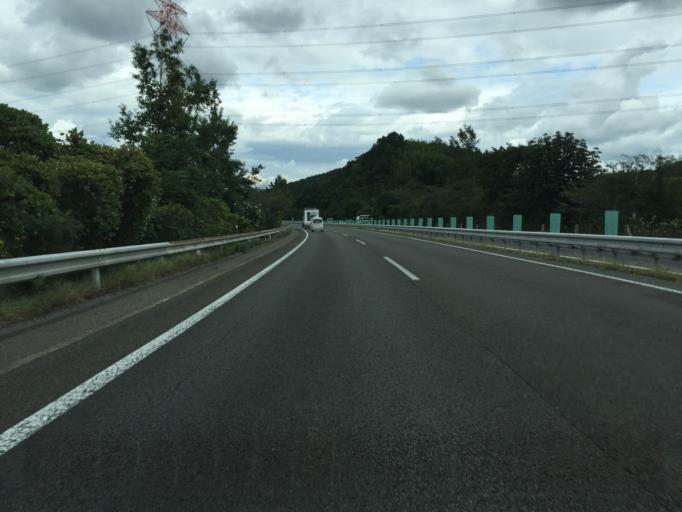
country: JP
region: Miyagi
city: Shiroishi
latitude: 37.9577
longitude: 140.6198
